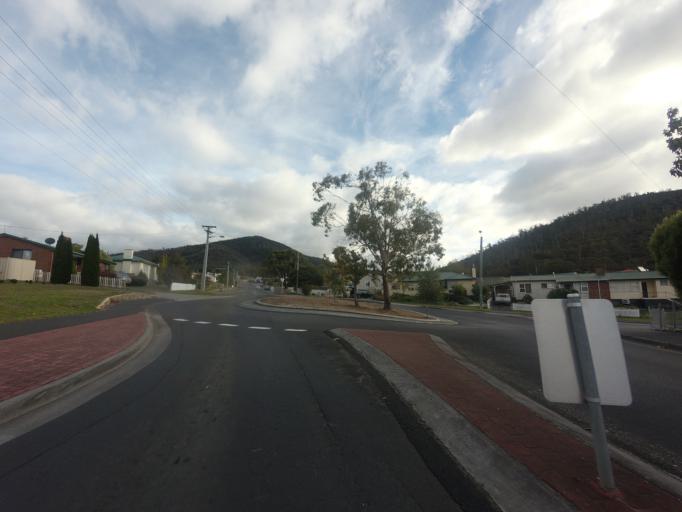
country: AU
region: Tasmania
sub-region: Glenorchy
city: Berriedale
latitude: -42.8097
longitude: 147.2434
